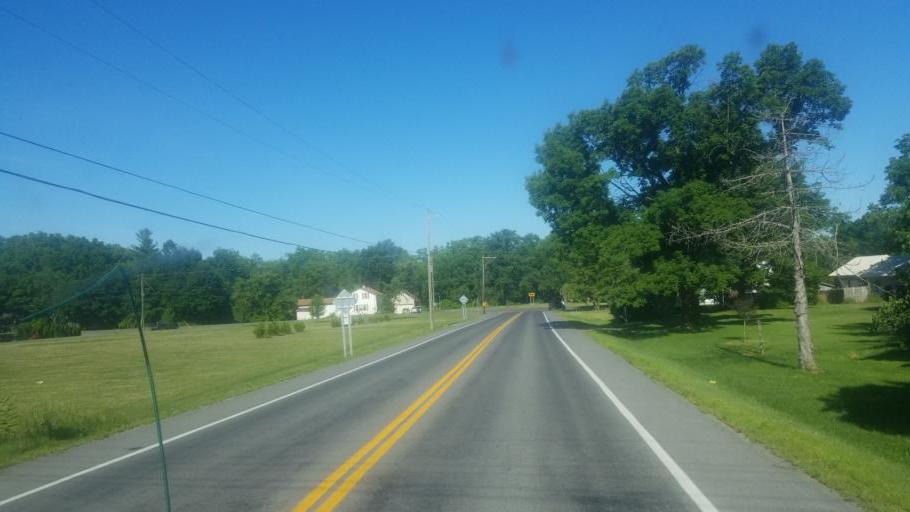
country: US
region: New York
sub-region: Ontario County
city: Canandaigua
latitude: 42.8363
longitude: -77.2130
